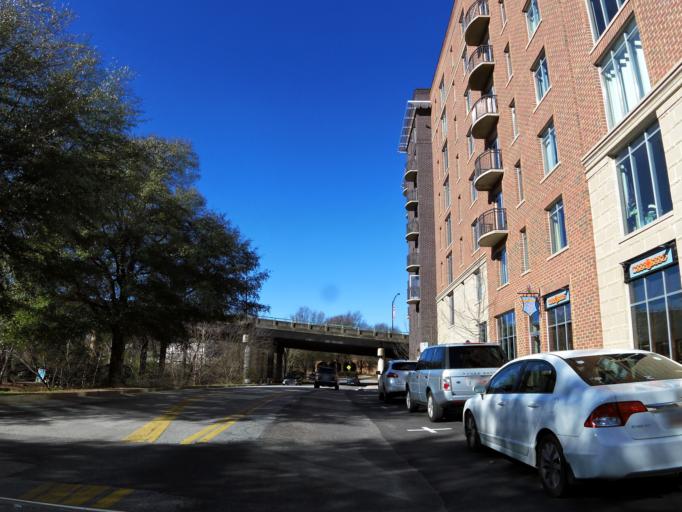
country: US
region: South Carolina
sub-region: Greenville County
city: Greenville
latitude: 34.8489
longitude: -82.4030
